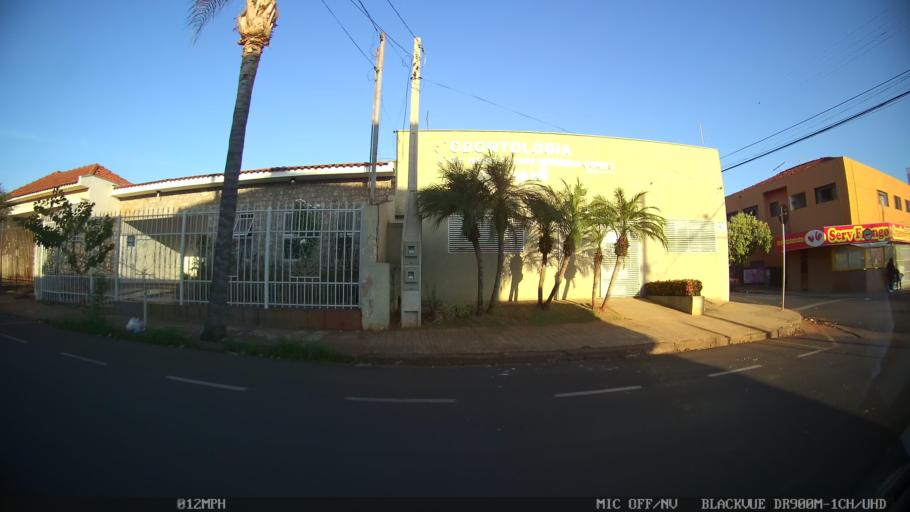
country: BR
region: Sao Paulo
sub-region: Sao Jose Do Rio Preto
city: Sao Jose do Rio Preto
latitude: -20.7981
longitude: -49.3697
